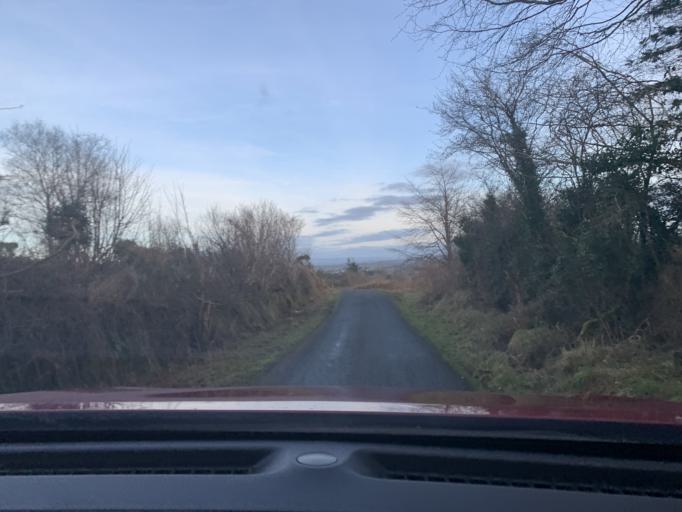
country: IE
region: Connaught
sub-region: Sligo
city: Strandhill
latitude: 54.1771
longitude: -8.6335
